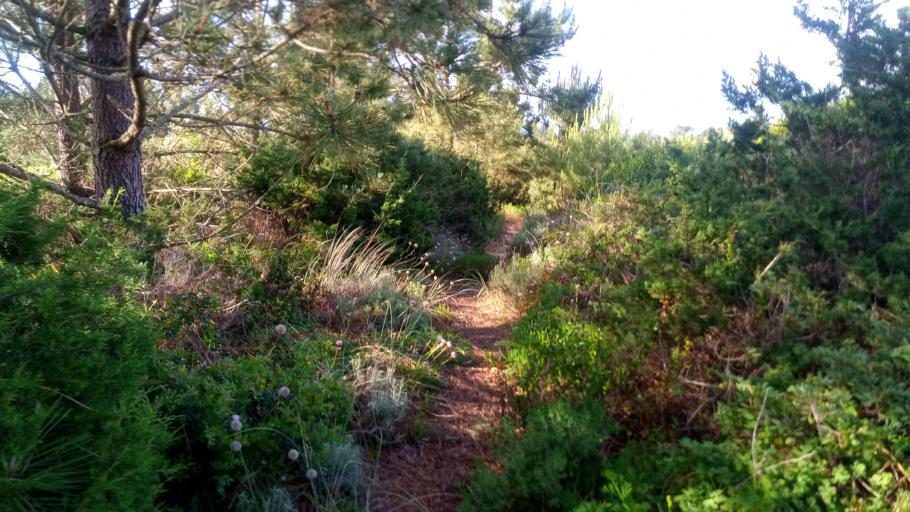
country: PT
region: Leiria
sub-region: Caldas da Rainha
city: Caldas da Rainha
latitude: 39.5036
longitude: -9.1532
